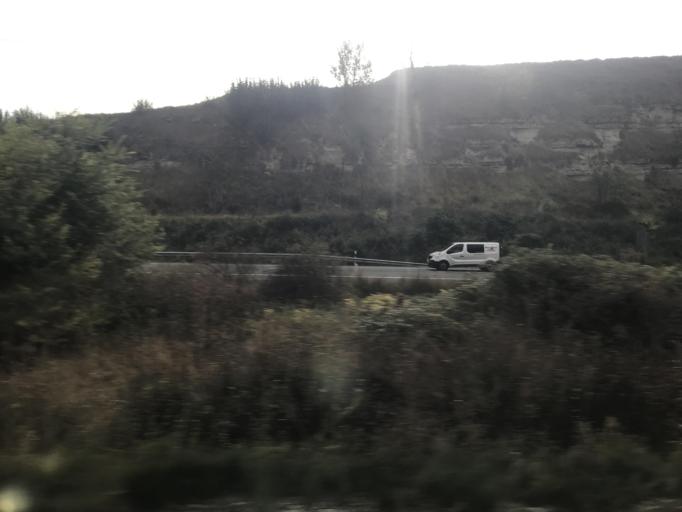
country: ES
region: Castille and Leon
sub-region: Provincia de Burgos
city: Briviesca
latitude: 42.5283
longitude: -3.3283
